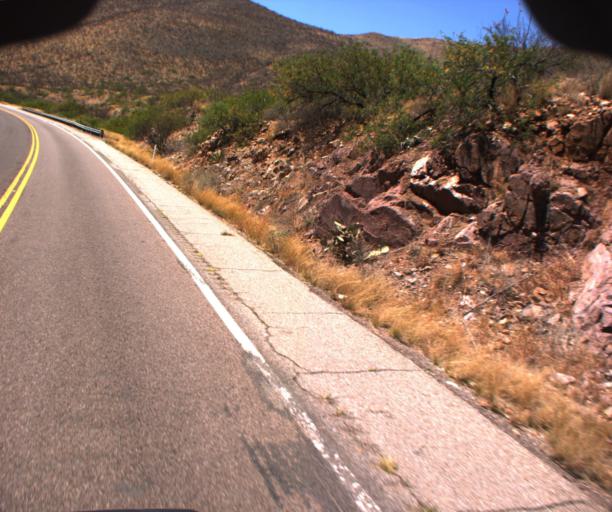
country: US
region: Arizona
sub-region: Cochise County
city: Bisbee
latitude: 31.4437
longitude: -109.8335
